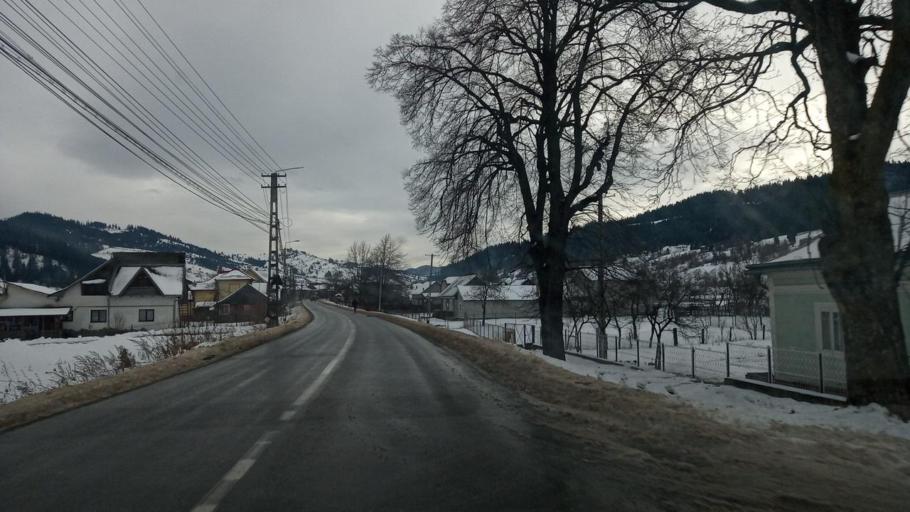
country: RO
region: Suceava
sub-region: Comuna Frasin
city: Frasin
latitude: 47.5280
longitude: 25.7978
